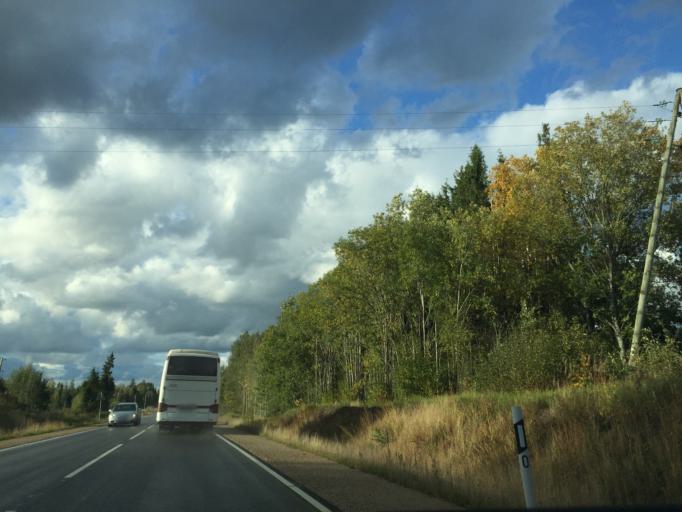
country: LV
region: Ligatne
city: Ligatne
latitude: 57.1448
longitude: 25.0780
